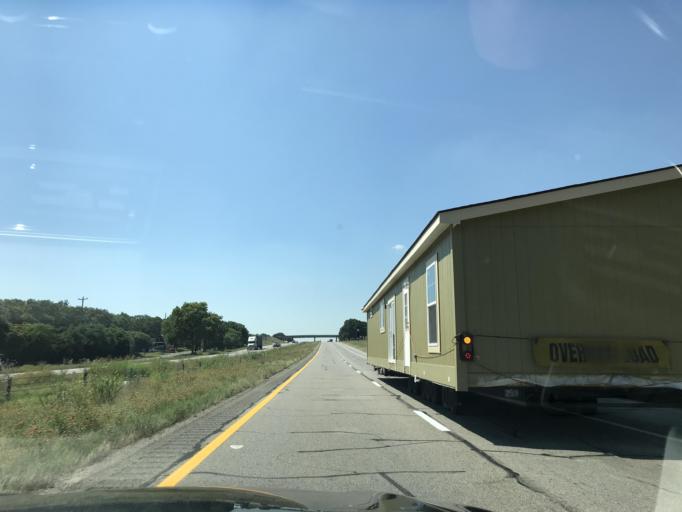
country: US
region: Texas
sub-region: Johnson County
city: Alvarado
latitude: 32.3849
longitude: -97.2072
